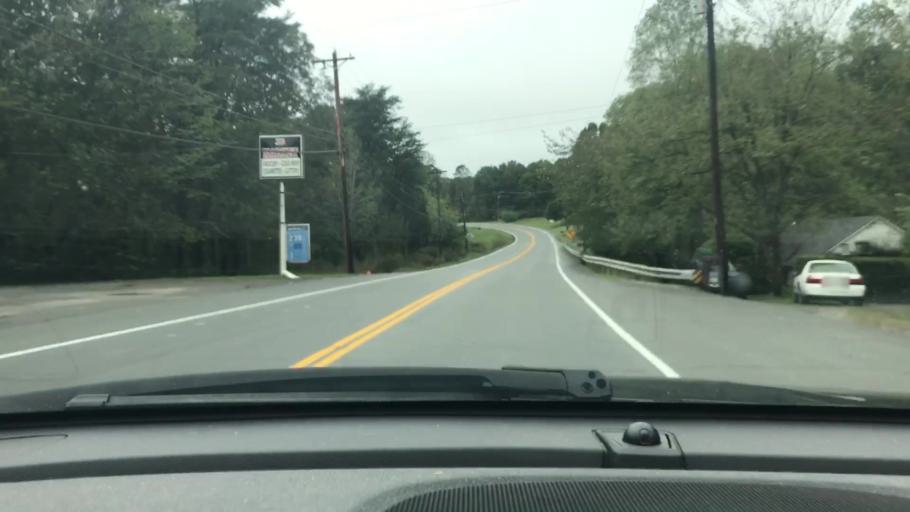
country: US
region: Tennessee
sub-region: Cheatham County
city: Kingston Springs
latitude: 36.1133
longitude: -87.1490
